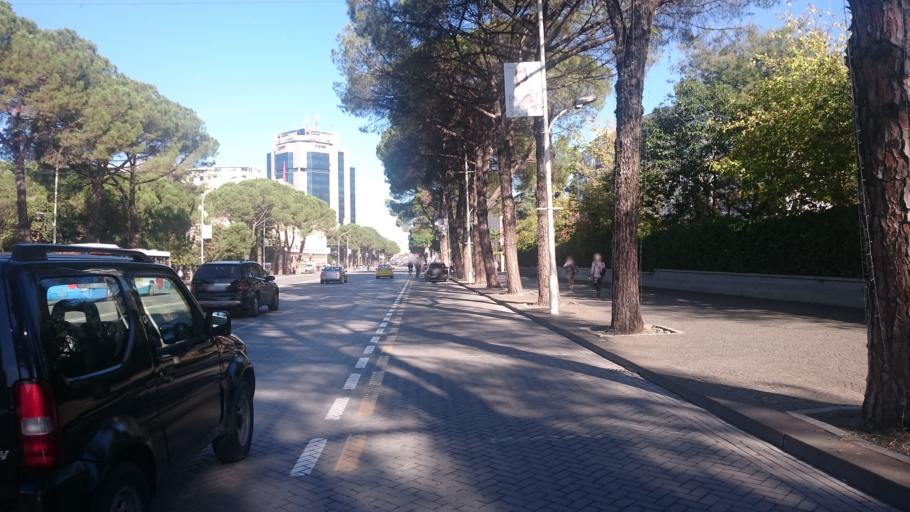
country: AL
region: Tirane
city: Tirana
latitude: 41.3199
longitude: 19.8209
